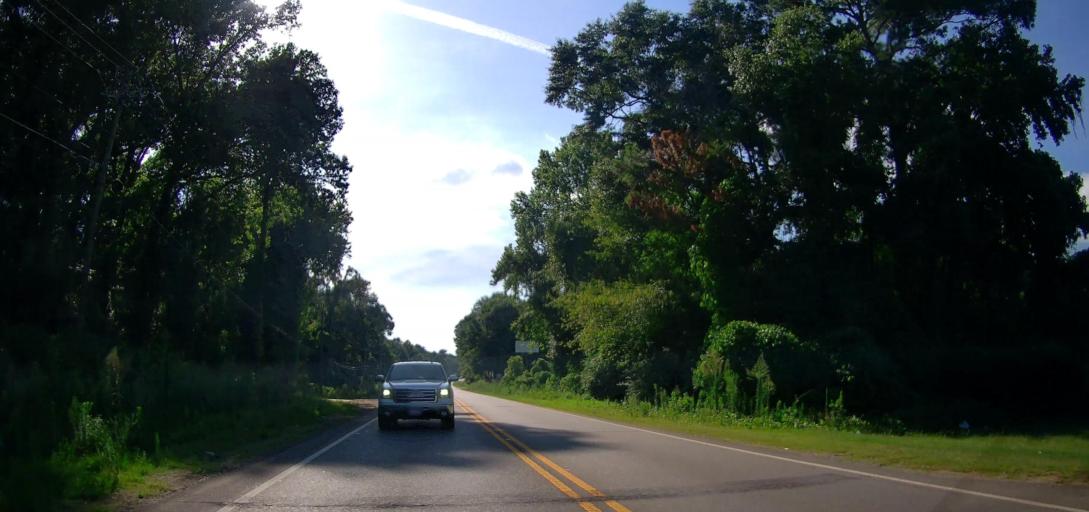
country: US
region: Alabama
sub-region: Tuscaloosa County
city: Holt
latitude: 33.1928
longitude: -87.4694
